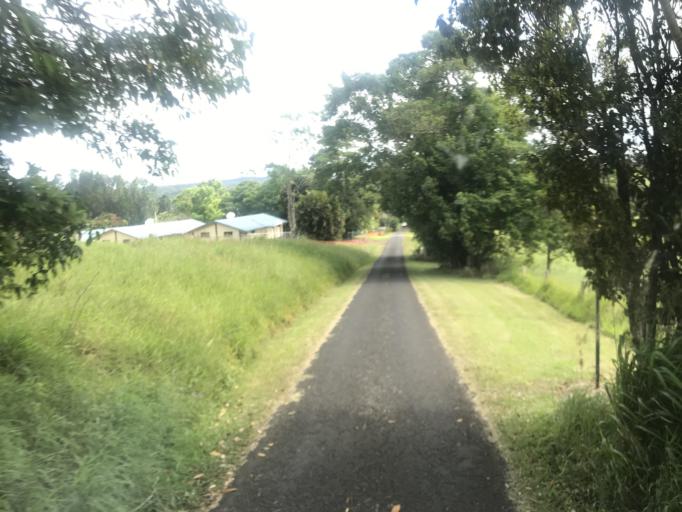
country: AU
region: Queensland
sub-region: Tablelands
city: Ravenshoe
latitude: -17.5483
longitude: 145.6980
